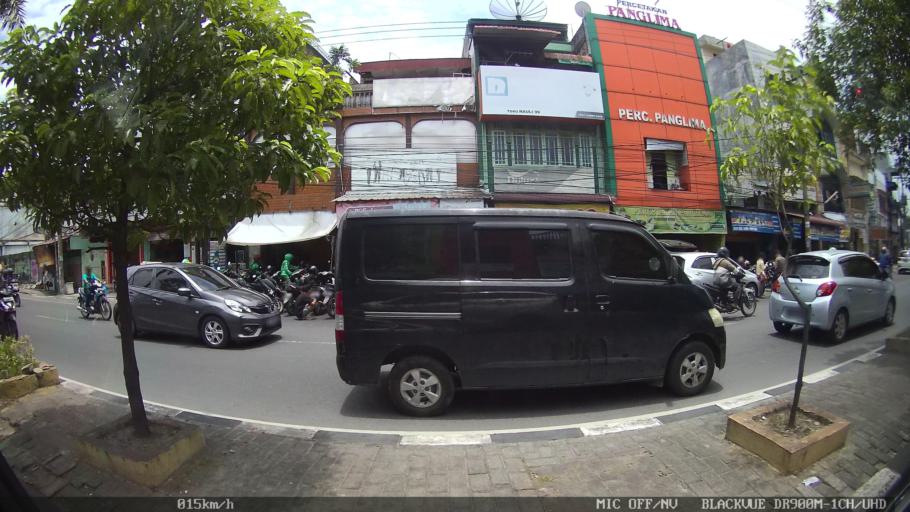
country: ID
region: North Sumatra
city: Medan
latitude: 3.5688
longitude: 98.6599
